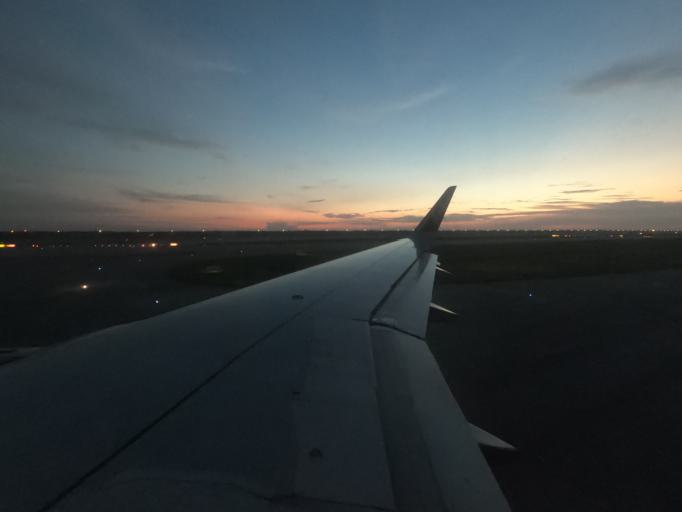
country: MY
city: Sungai Pelek New Village
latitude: 2.7190
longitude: 101.6936
